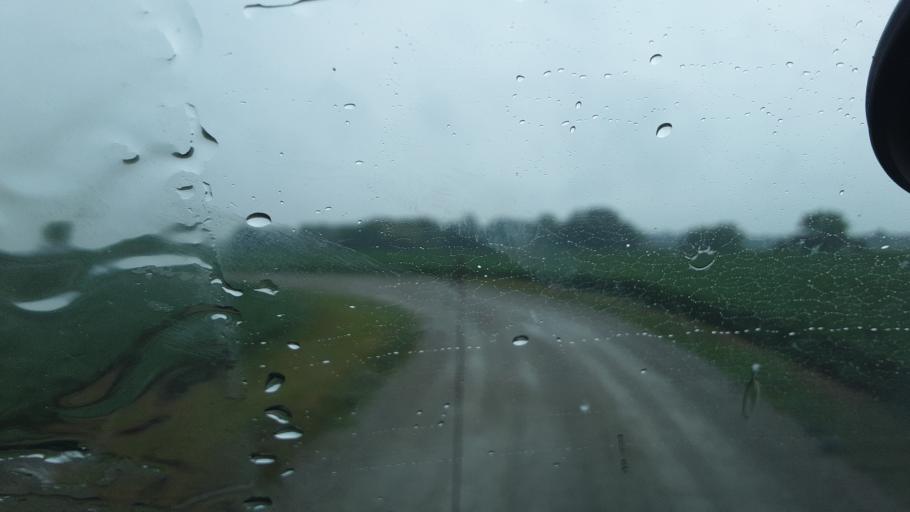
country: US
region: Ohio
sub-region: Williams County
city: Edgerton
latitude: 41.4084
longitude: -84.8045
